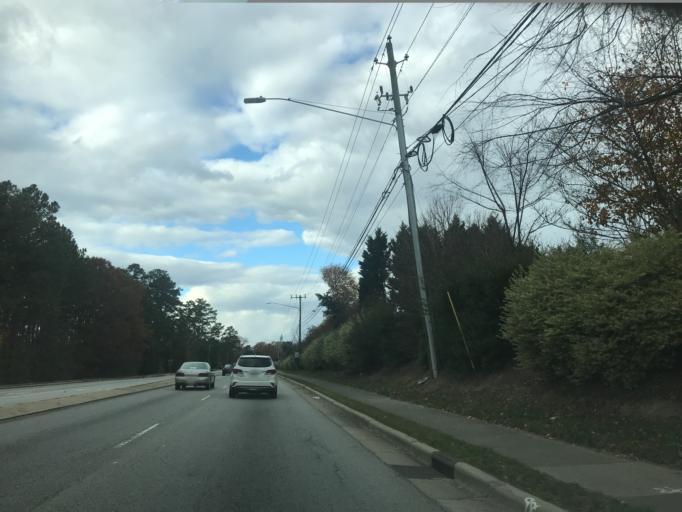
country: US
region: North Carolina
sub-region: Wake County
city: Raleigh
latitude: 35.8167
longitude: -78.5676
